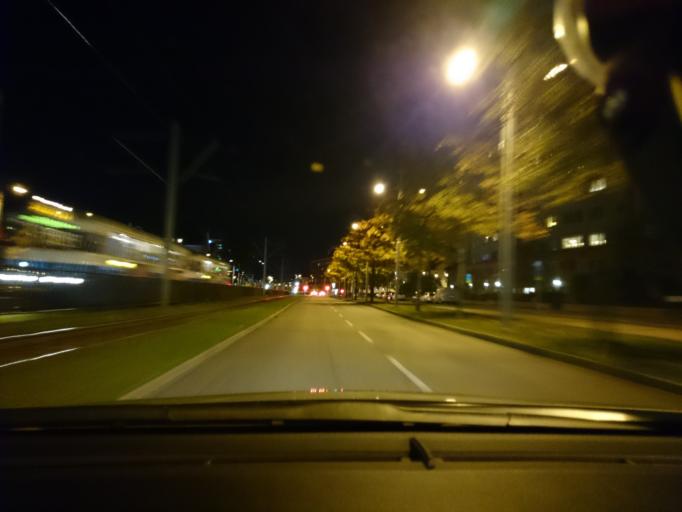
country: SE
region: Vaestra Goetaland
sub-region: Goteborg
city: Goeteborg
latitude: 57.6888
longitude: 11.9950
